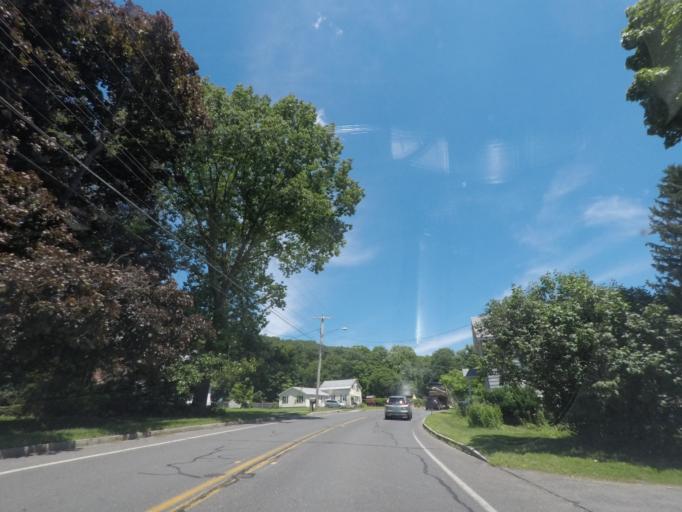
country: US
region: Massachusetts
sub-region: Berkshire County
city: Lee
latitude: 42.2969
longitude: -73.2248
